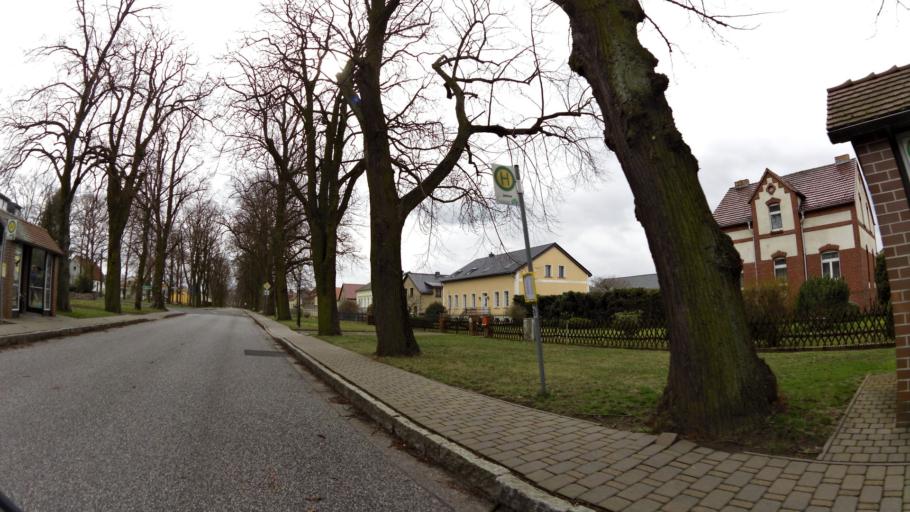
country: DE
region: Brandenburg
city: Rangsdorf
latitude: 52.3245
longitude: 13.4634
